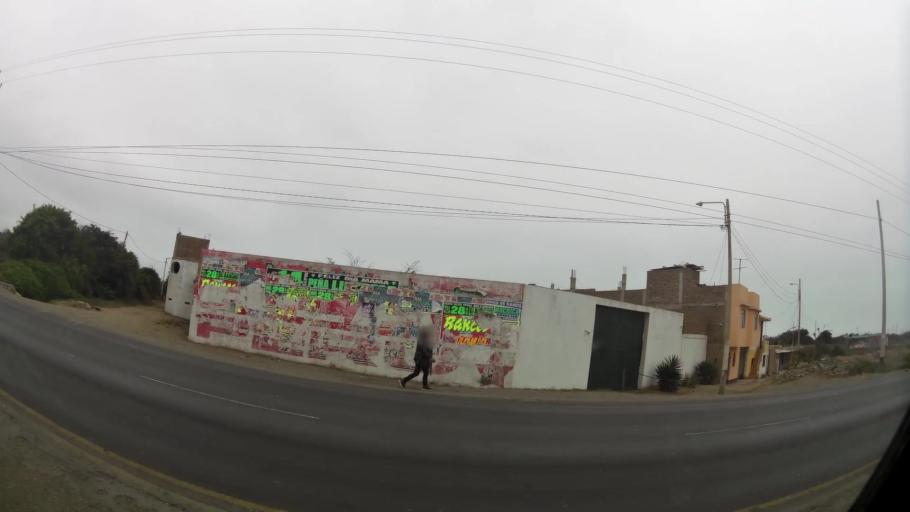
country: PE
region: La Libertad
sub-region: Provincia de Trujillo
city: Moche
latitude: -8.1720
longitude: -79.0008
